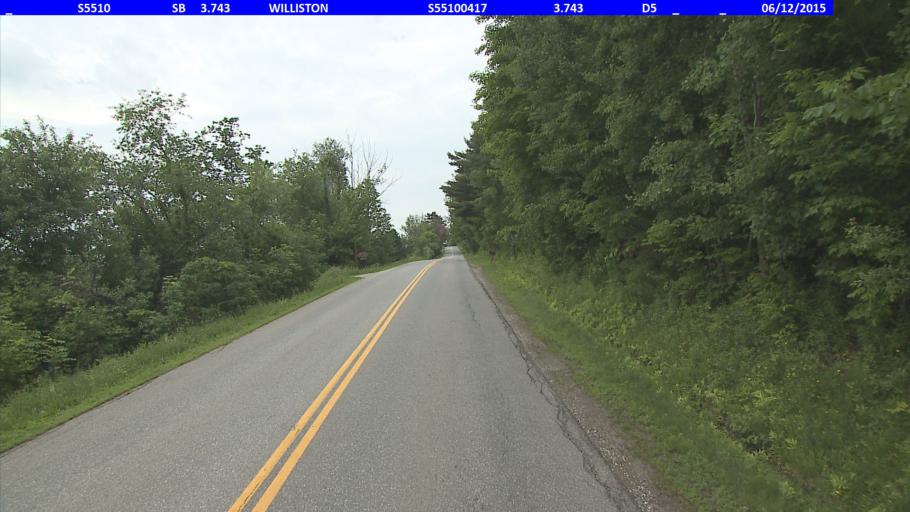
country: US
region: Vermont
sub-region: Chittenden County
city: Williston
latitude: 44.4235
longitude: -73.0789
